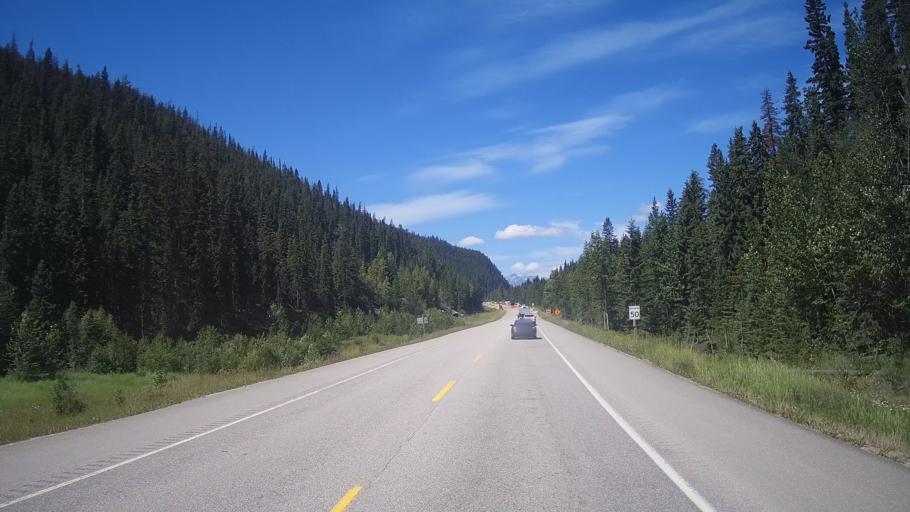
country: CA
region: Alberta
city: Jasper Park Lodge
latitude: 52.8651
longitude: -118.2396
